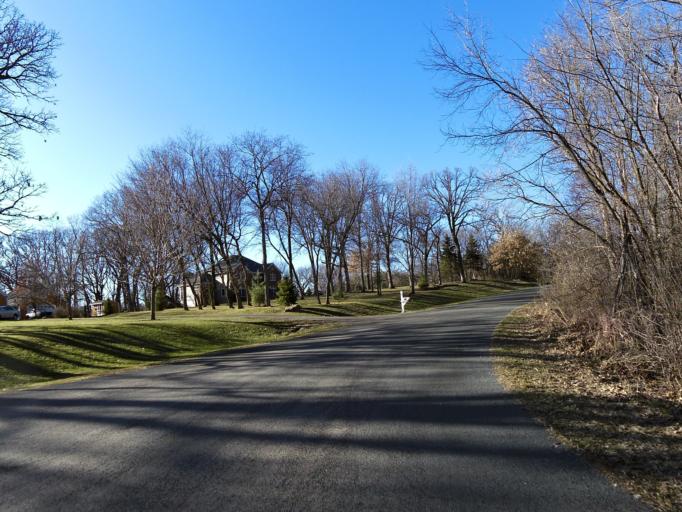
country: US
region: Minnesota
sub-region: Washington County
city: Lakeland
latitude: 44.9813
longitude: -92.8020
